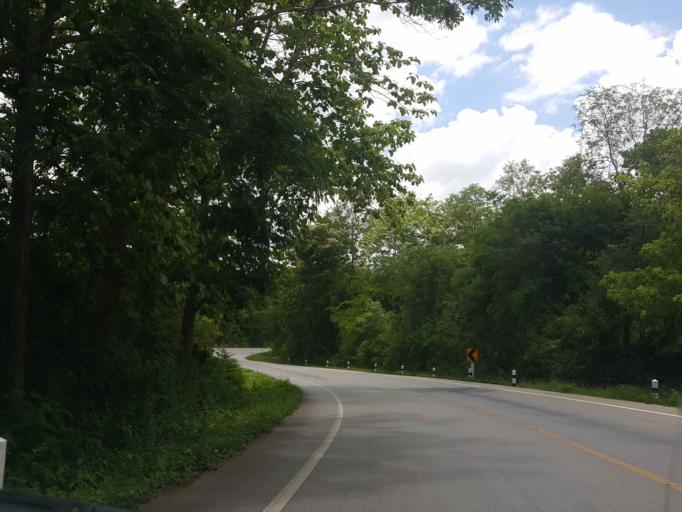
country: TH
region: Nan
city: Wiang Sa
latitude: 18.5181
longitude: 100.5907
